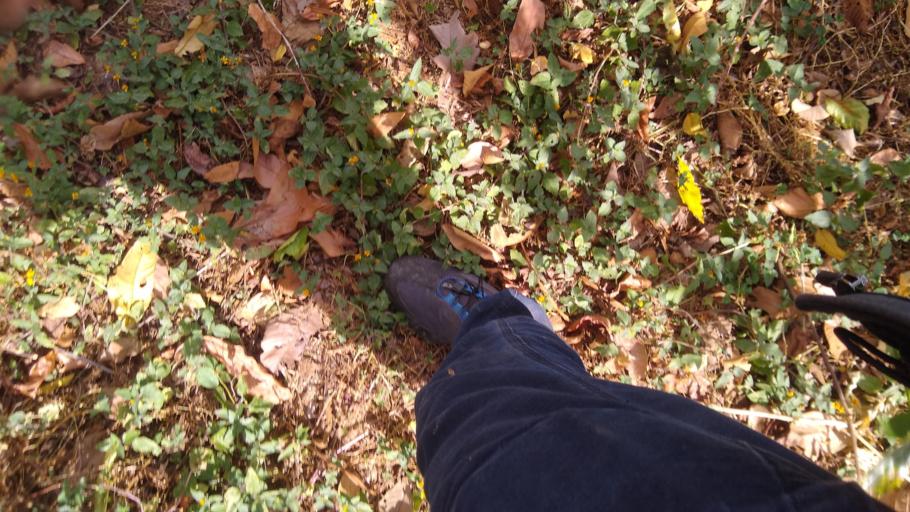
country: MX
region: Puebla
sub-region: Tepetzintla
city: Tlamanca de Hernandez
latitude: 19.9337
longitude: -97.8153
